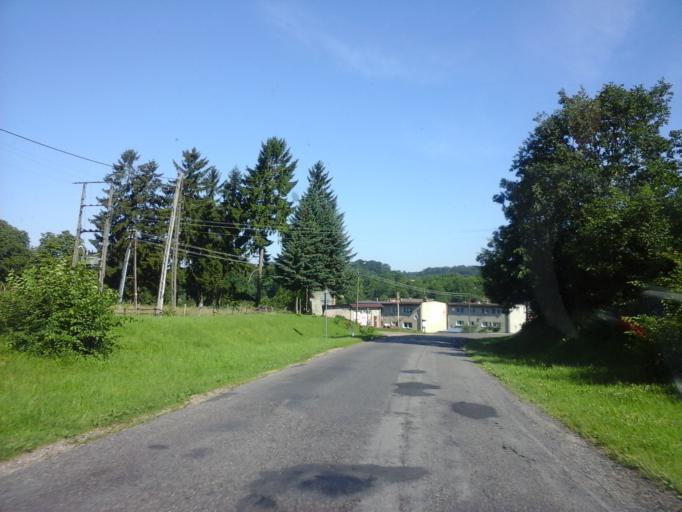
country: PL
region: West Pomeranian Voivodeship
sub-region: Powiat swidwinski
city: Polczyn-Zdroj
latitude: 53.6726
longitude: 16.0185
